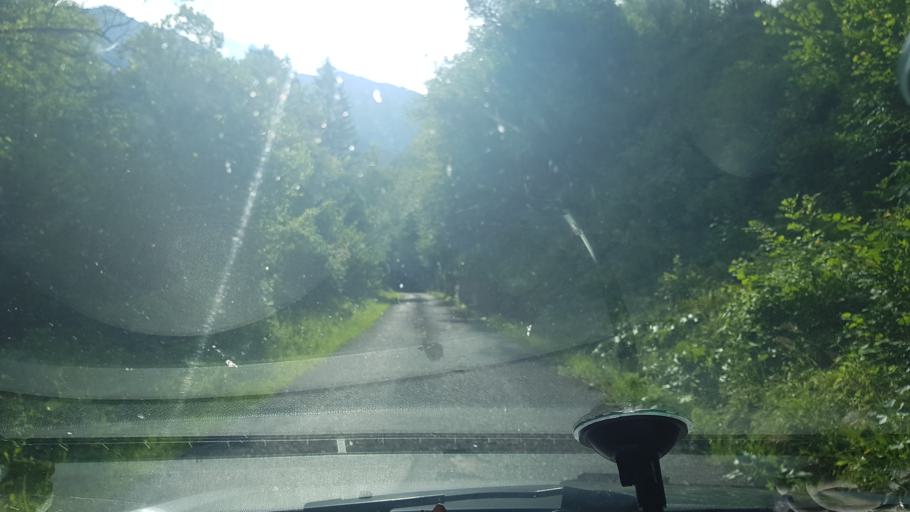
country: IT
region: Friuli Venezia Giulia
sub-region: Provincia di Udine
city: Prato
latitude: 46.3488
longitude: 13.3907
